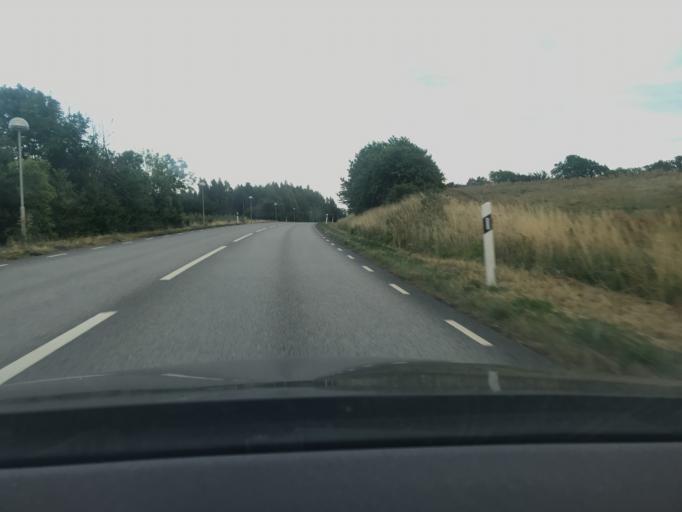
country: SE
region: Skane
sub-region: Simrishamns Kommun
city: Simrishamn
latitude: 55.5876
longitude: 14.3220
